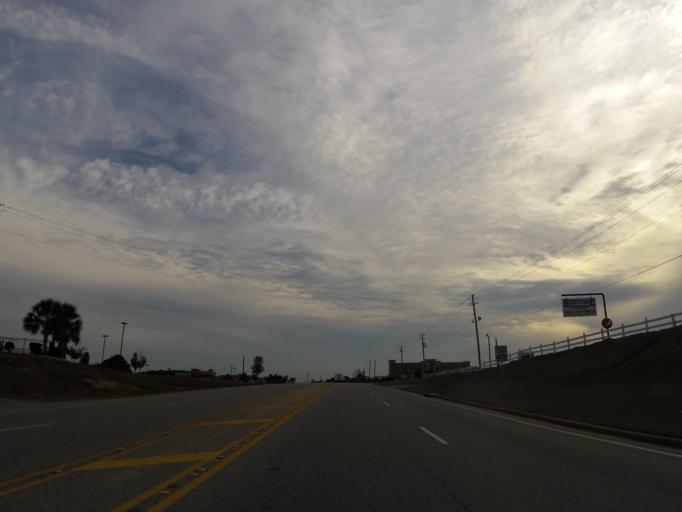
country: US
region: Alabama
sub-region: Escambia County
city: Atmore
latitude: 31.1085
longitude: -87.4754
